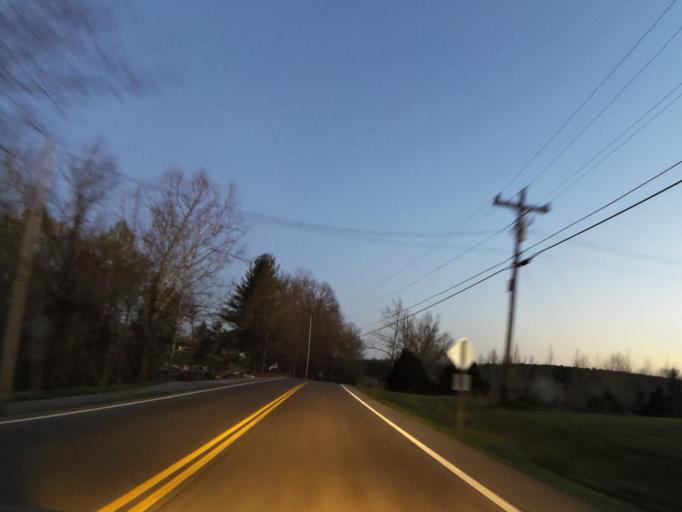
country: US
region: Tennessee
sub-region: Robertson County
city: Coopertown
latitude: 36.3955
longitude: -86.9011
